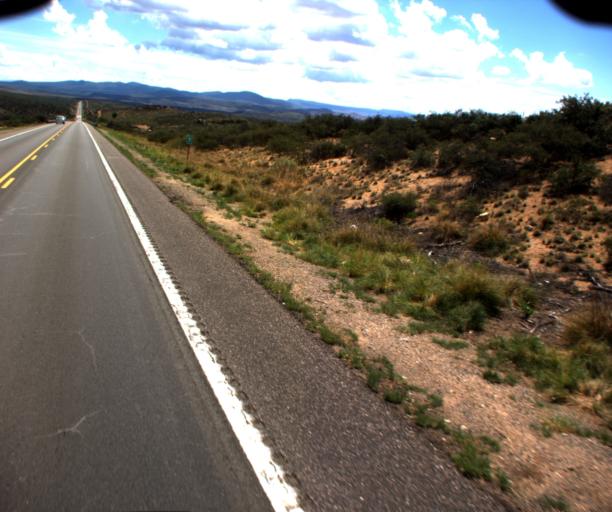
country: US
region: Arizona
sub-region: Yavapai County
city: Dewey-Humboldt
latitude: 34.5334
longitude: -112.1289
